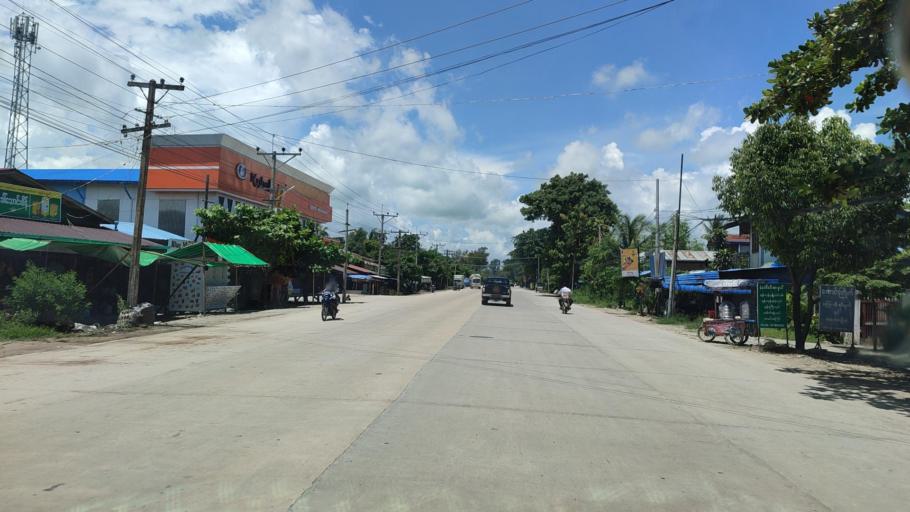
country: MM
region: Bago
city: Taungoo
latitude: 18.9048
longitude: 96.4380
